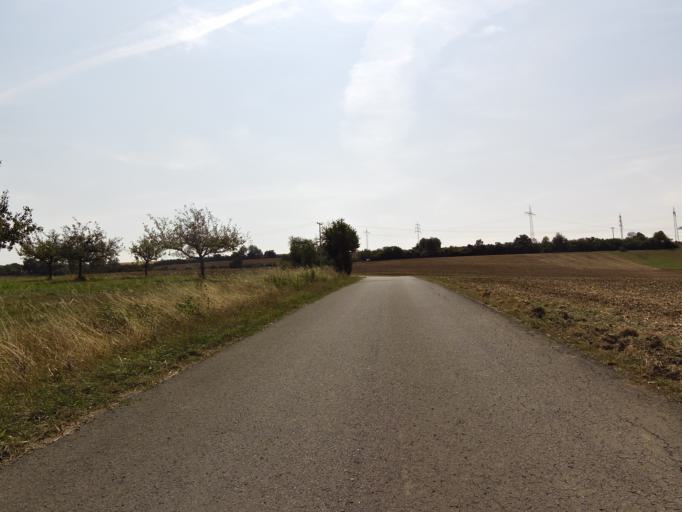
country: DE
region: Bavaria
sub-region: Regierungsbezirk Unterfranken
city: Rottendorf
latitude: 49.7843
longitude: 10.0301
